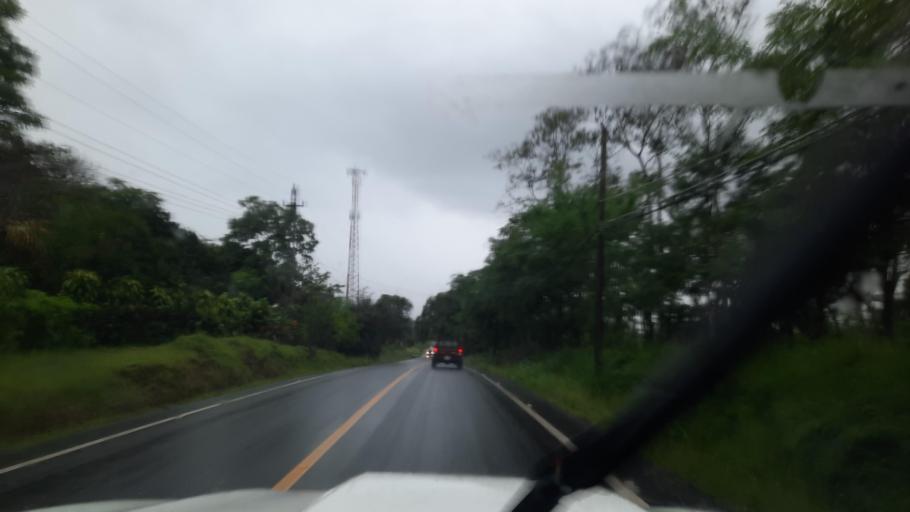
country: PA
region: Chiriqui
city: Sortova
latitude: 8.5548
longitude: -82.6268
